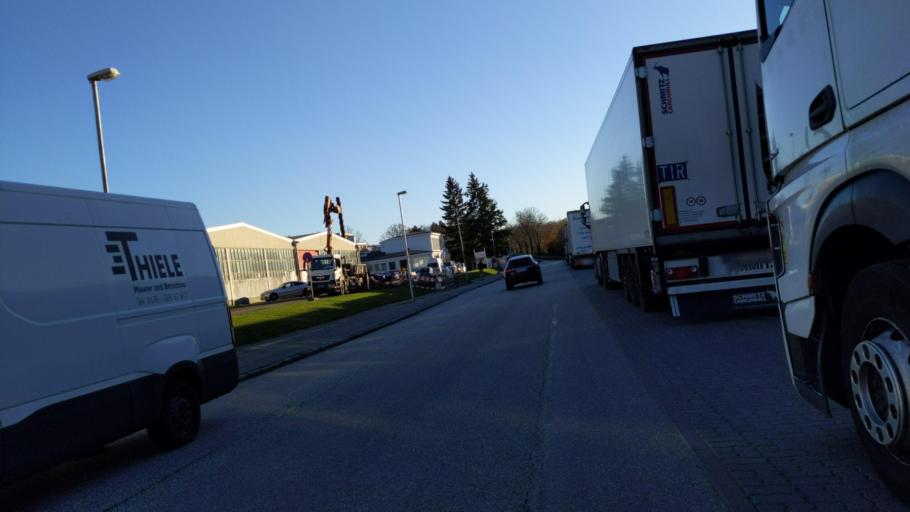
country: DE
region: Schleswig-Holstein
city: Bad Schwartau
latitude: 53.8938
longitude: 10.7070
